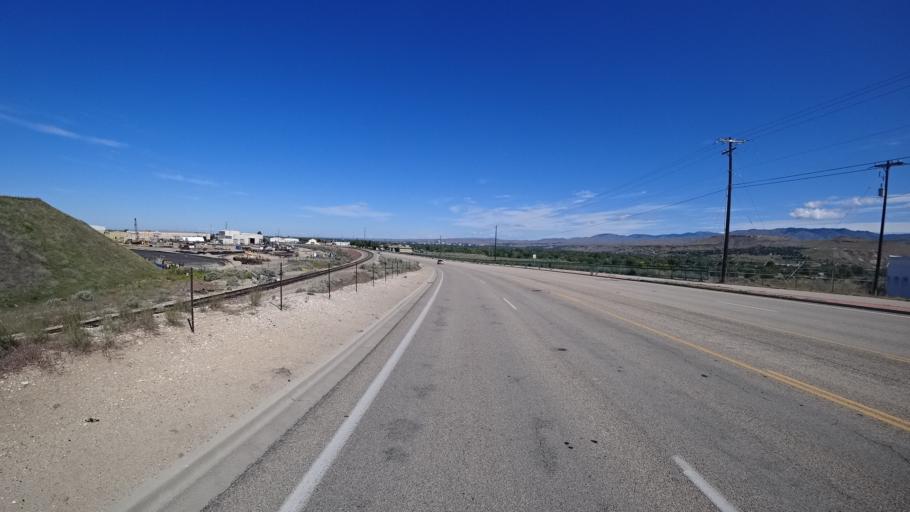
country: US
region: Idaho
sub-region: Ada County
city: Boise
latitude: 43.5566
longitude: -116.1636
